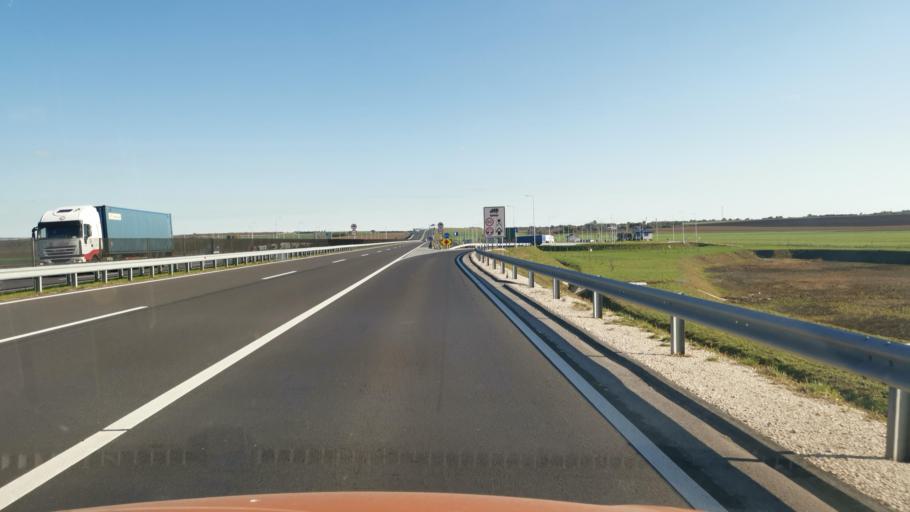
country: HU
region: Borsod-Abauj-Zemplen
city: Arnot
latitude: 48.1529
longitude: 20.8690
